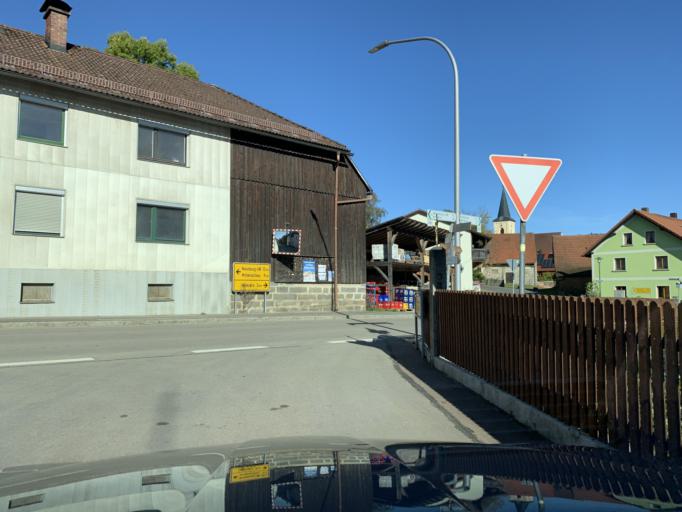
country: DE
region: Bavaria
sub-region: Upper Palatinate
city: Thanstein
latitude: 49.4058
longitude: 12.4626
